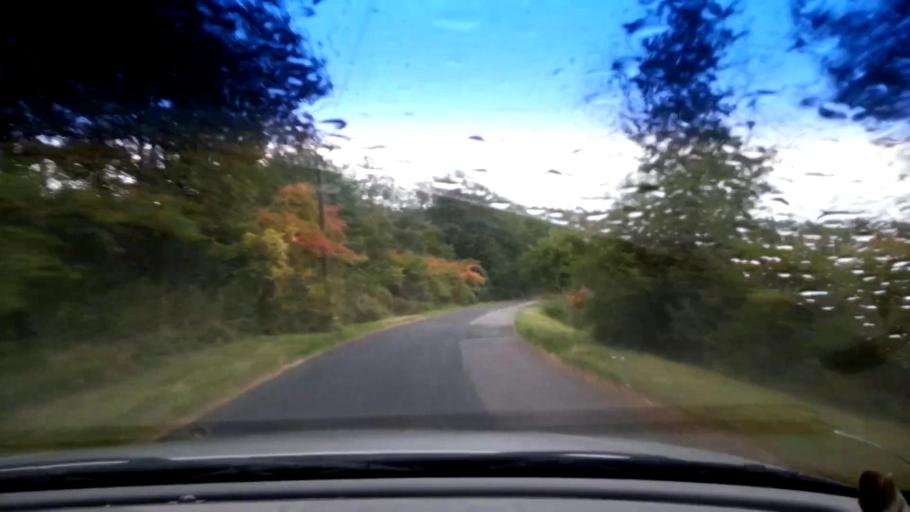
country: DE
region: Bavaria
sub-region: Upper Franconia
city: Priesendorf
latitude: 49.8776
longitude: 10.6678
